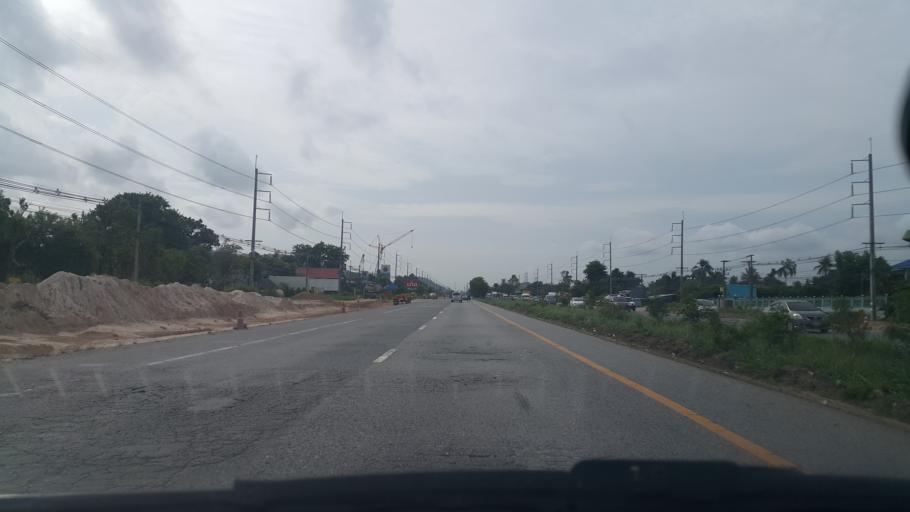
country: TH
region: Rayong
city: Nikhom Phattana
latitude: 12.8002
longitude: 101.1484
